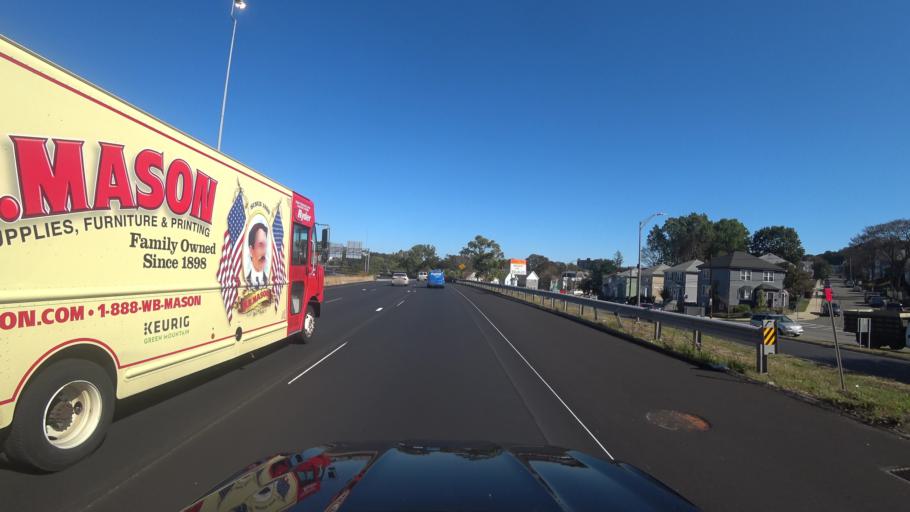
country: US
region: Massachusetts
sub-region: Suffolk County
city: Chelsea
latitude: 42.4034
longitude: -71.0306
